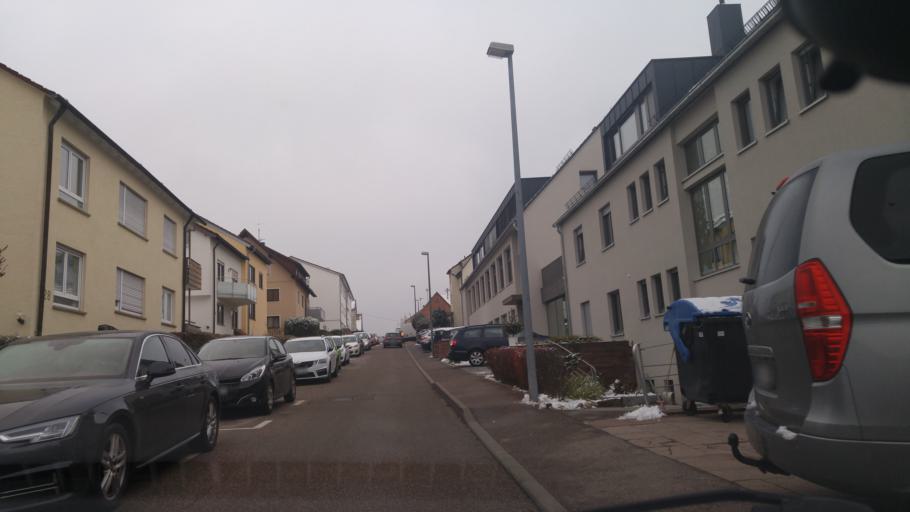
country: DE
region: Baden-Wuerttemberg
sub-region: Regierungsbezirk Stuttgart
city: Leonberg
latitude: 48.8056
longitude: 9.0130
